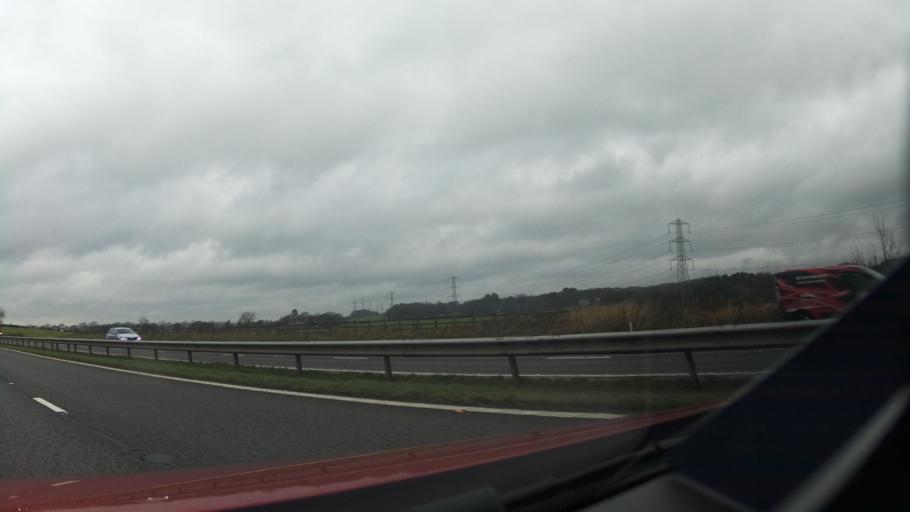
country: GB
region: England
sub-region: Lancashire
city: Bay Horse
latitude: 53.9684
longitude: -2.7666
